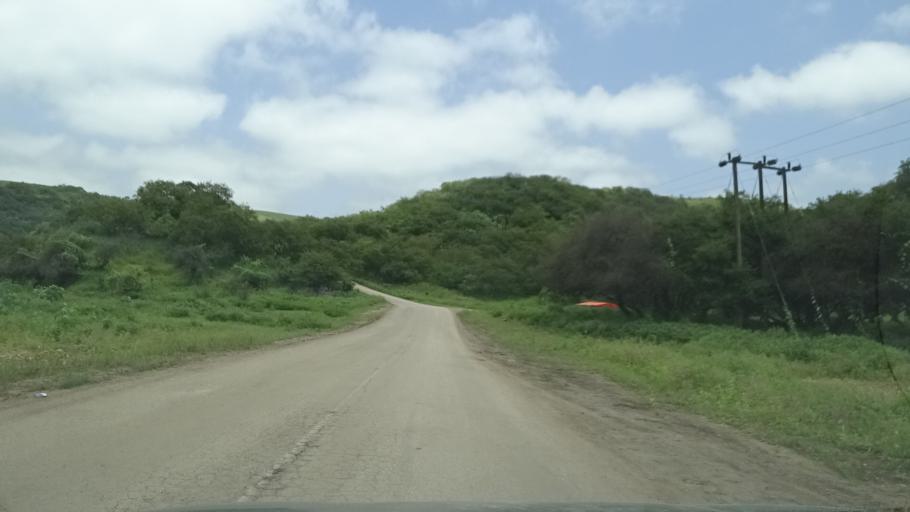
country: OM
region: Zufar
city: Salalah
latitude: 17.1986
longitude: 54.1815
